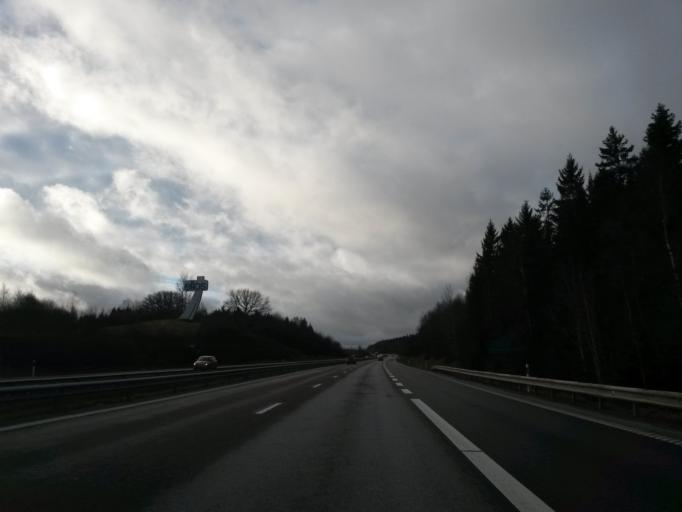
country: SE
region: Vaestra Goetaland
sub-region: Boras Kommun
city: Sjomarken
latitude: 57.6964
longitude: 12.8175
